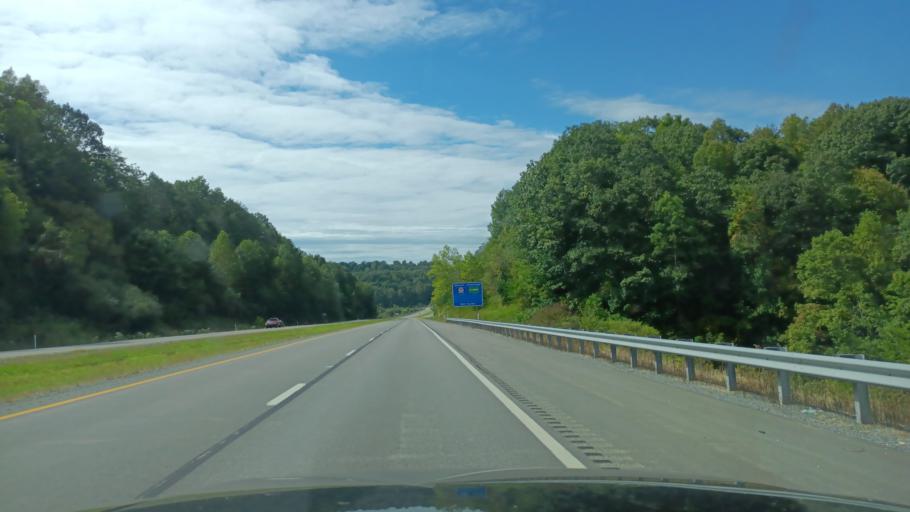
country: US
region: West Virginia
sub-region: Ritchie County
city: Pennsboro
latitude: 39.2747
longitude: -80.9797
